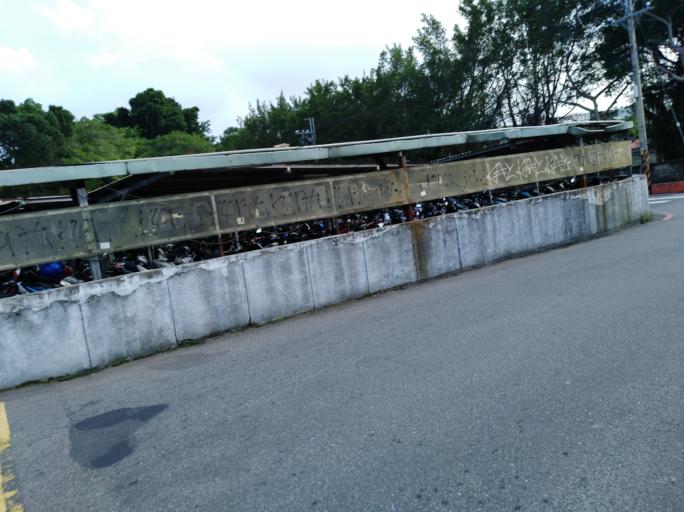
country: TW
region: Taipei
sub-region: Taipei
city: Banqiao
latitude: 25.0362
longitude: 121.4285
